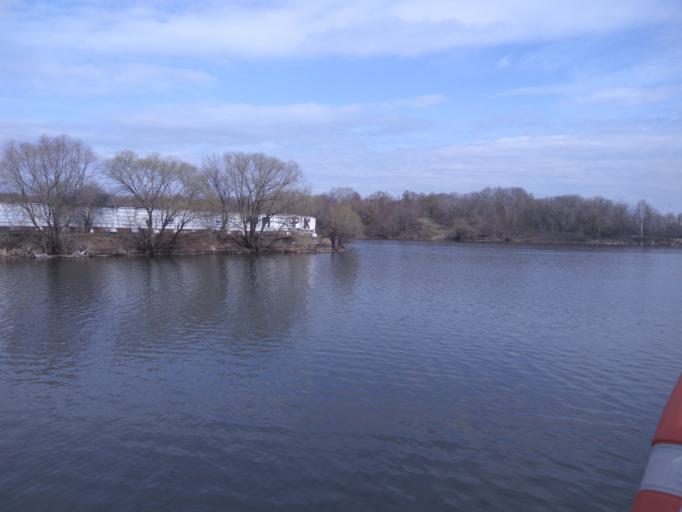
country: RU
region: Moscow
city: Kolomenskoye
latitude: 55.6885
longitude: 37.7038
